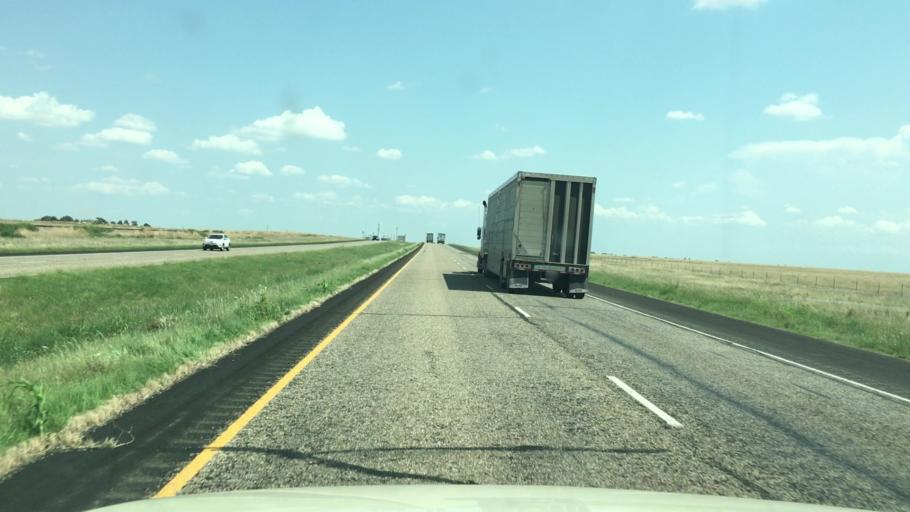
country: US
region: Texas
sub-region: Armstrong County
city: Claude
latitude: 35.1251
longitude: -101.3962
